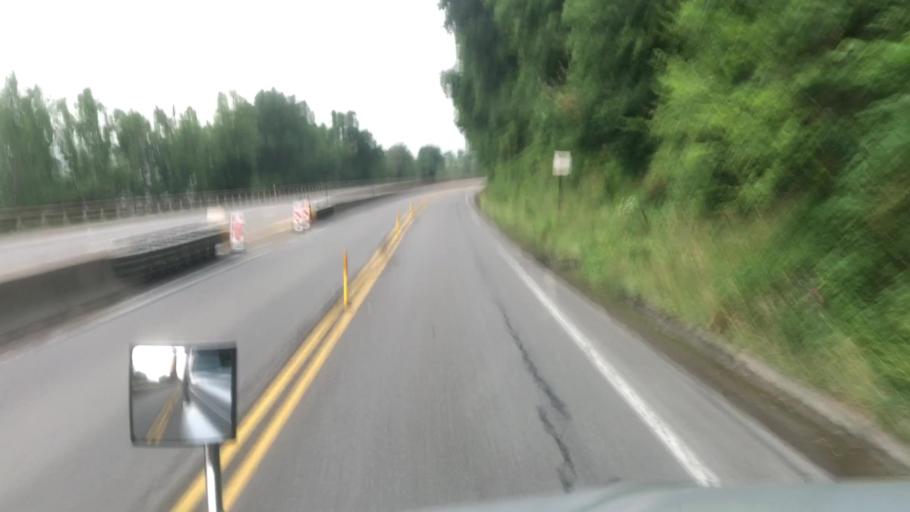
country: US
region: Pennsylvania
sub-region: Venango County
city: Woodland Heights
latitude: 41.4144
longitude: -79.7330
